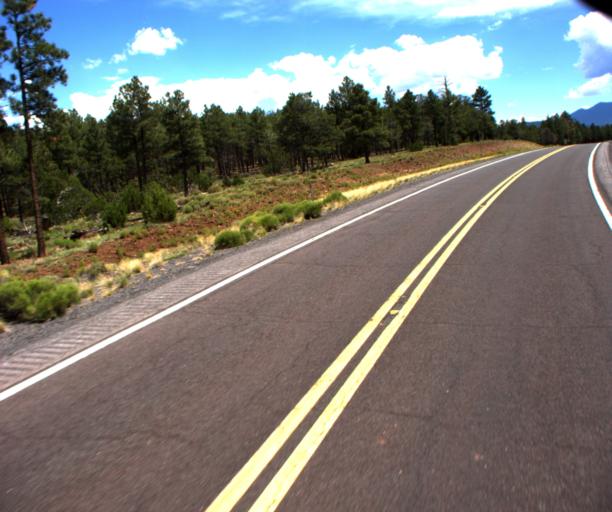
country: US
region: Arizona
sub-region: Coconino County
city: Parks
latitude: 35.5077
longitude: -111.8252
